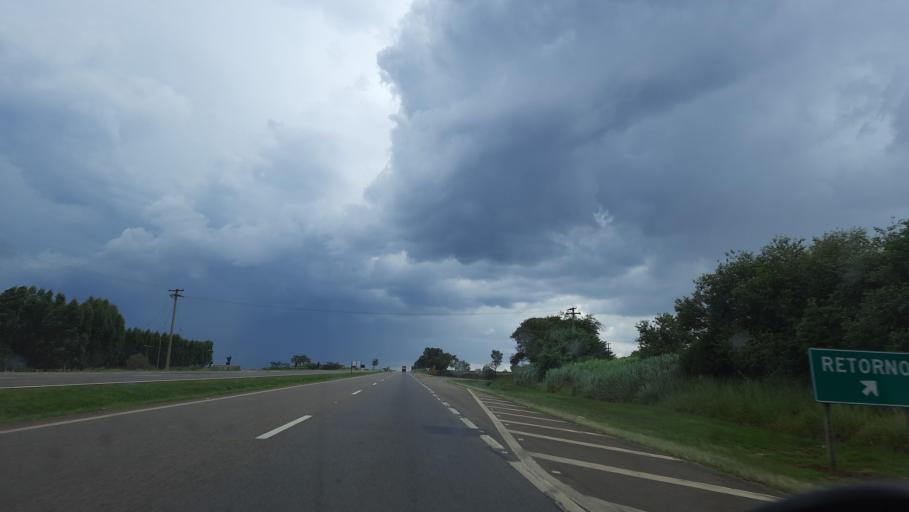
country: BR
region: Sao Paulo
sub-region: Aguai
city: Aguai
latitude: -22.0130
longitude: -47.0359
